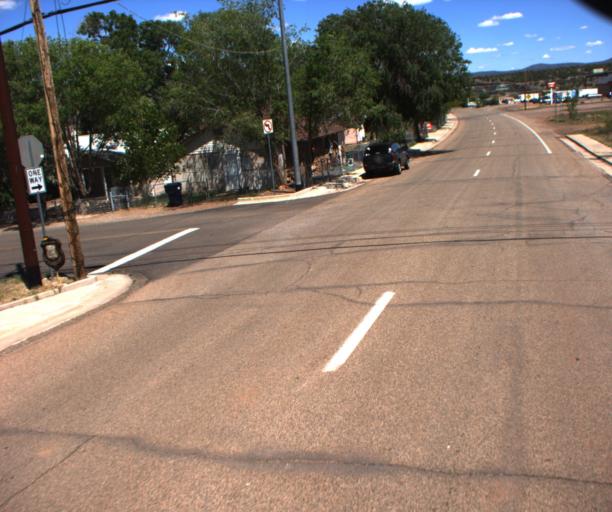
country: US
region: Arizona
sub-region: Coconino County
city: Williams
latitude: 35.2231
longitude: -112.4825
